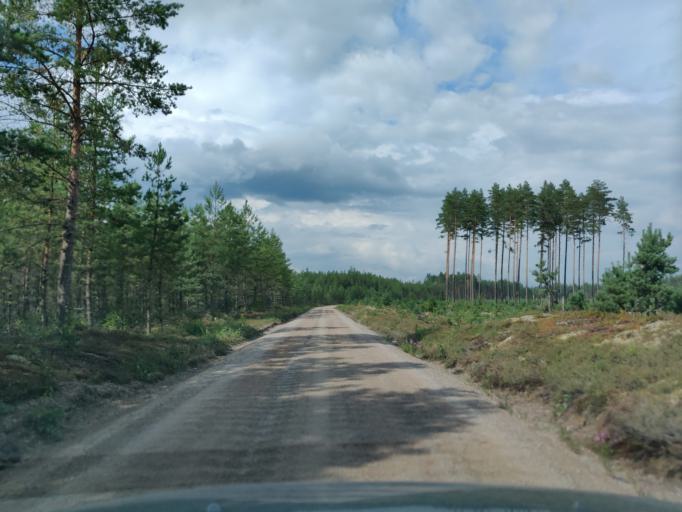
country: SE
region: Vaermland
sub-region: Hagfors Kommun
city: Hagfors
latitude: 59.9773
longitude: 13.5483
